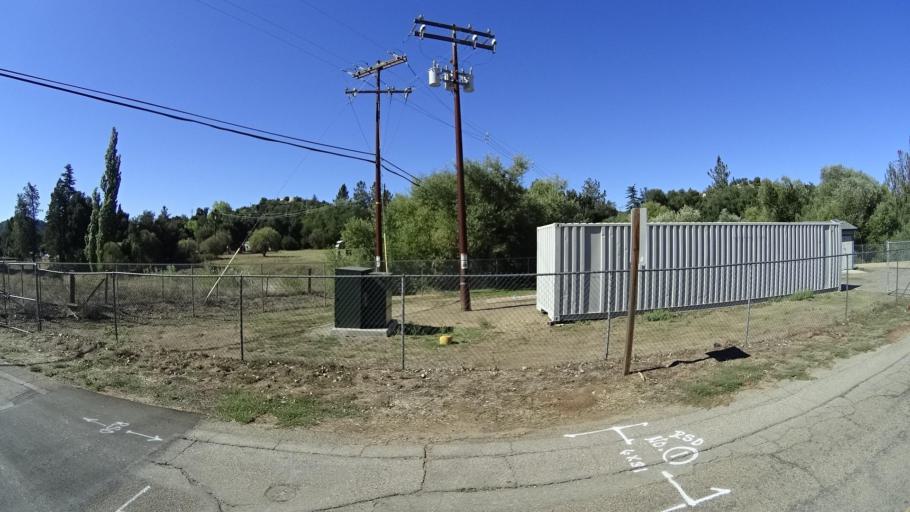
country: US
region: California
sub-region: San Diego County
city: Descanso
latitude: 32.8593
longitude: -116.6146
